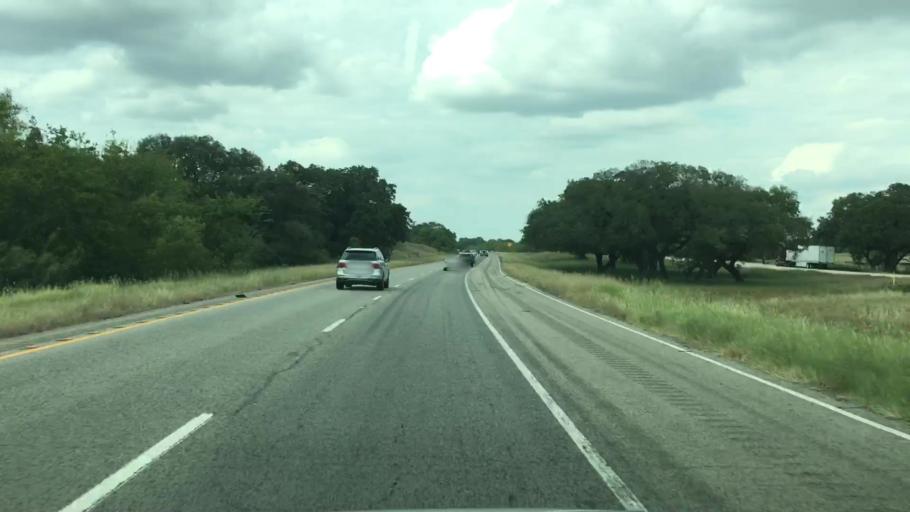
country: US
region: Texas
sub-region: Atascosa County
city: Pleasanton
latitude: 29.0342
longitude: -98.4324
